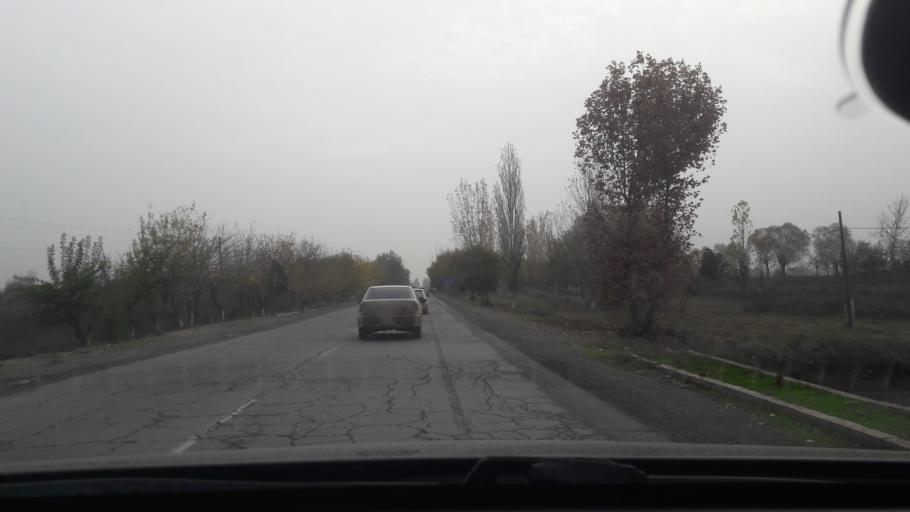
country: TJ
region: Khatlon
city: Qurghonteppa
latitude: 37.8652
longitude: 68.7171
